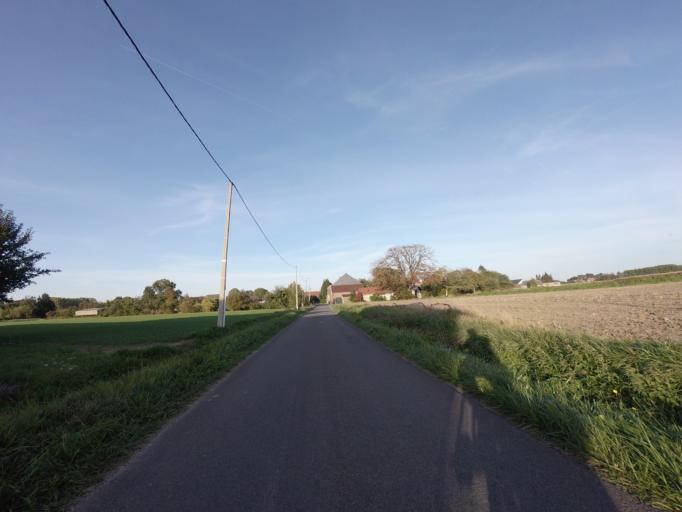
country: BE
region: Flanders
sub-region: Provincie Vlaams-Brabant
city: Kampenhout
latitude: 50.9360
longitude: 4.5914
